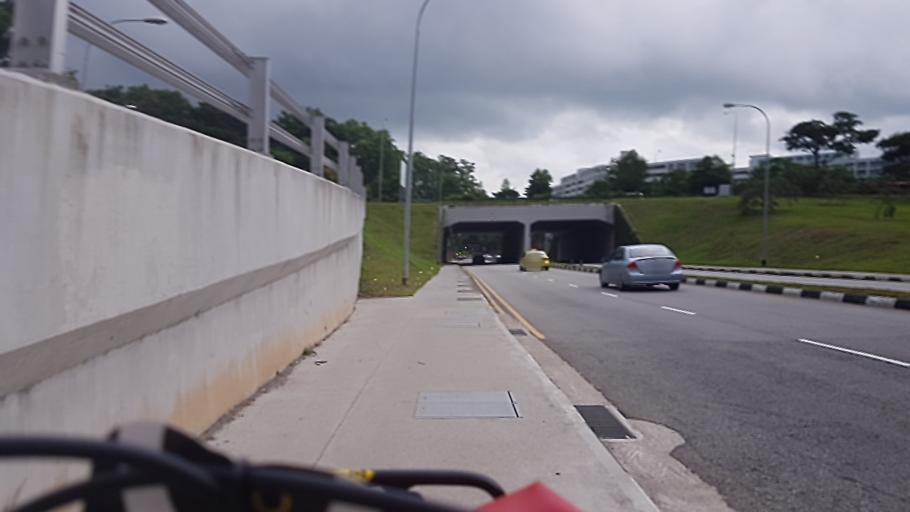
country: SG
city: Singapore
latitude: 1.3506
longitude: 103.9562
